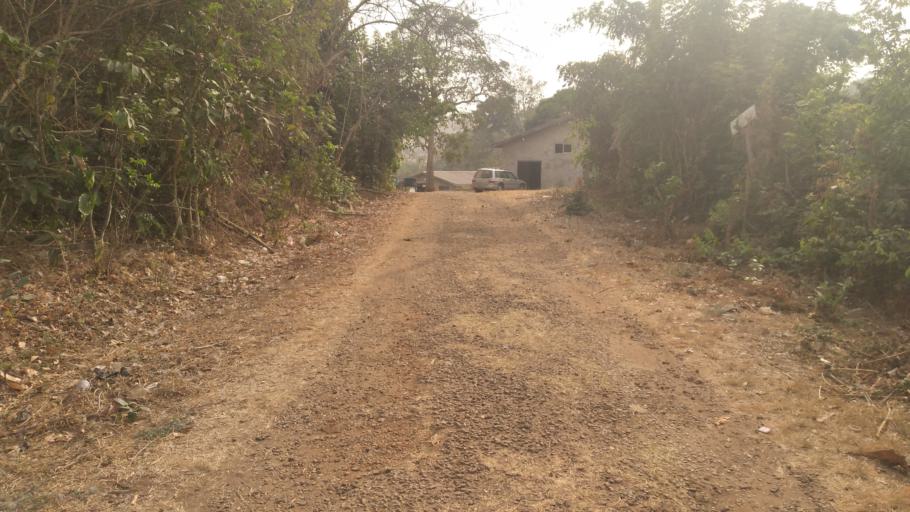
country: NG
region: Ondo
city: Akure
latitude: 7.2950
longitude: 5.1466
